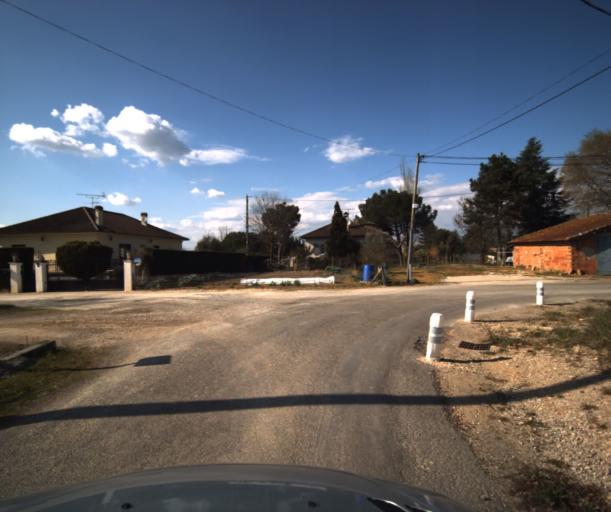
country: FR
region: Midi-Pyrenees
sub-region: Departement du Tarn-et-Garonne
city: Bressols
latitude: 43.9631
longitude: 1.3038
